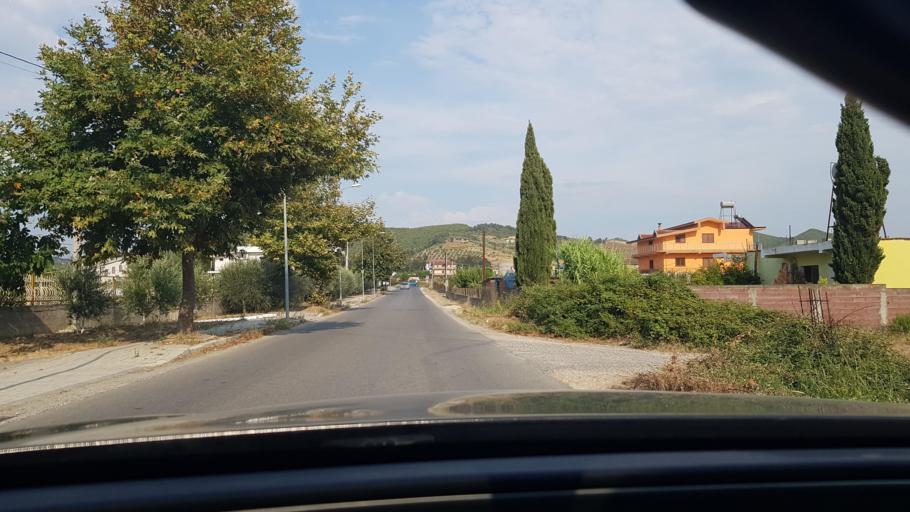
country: AL
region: Durres
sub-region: Rrethi i Durresit
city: Manze
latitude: 41.4746
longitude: 19.5592
